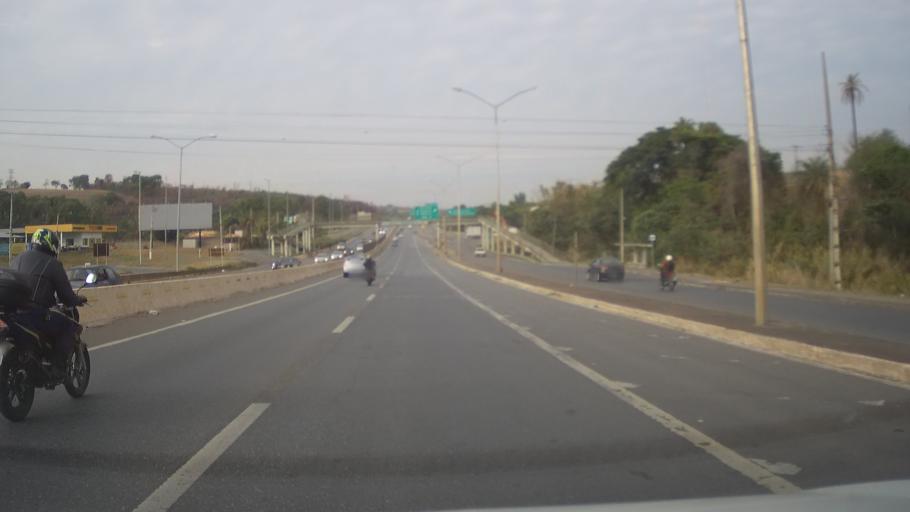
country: BR
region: Minas Gerais
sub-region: Vespasiano
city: Vespasiano
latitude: -19.7107
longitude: -43.9249
